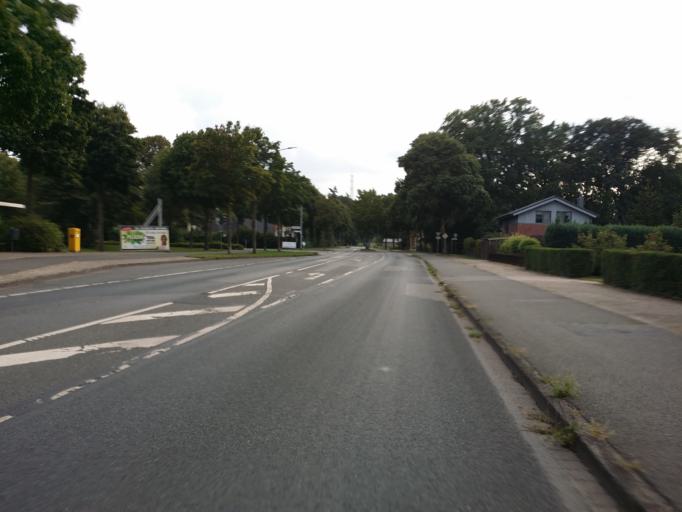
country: DE
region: Lower Saxony
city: Bremervorde
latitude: 53.4730
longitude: 9.1334
